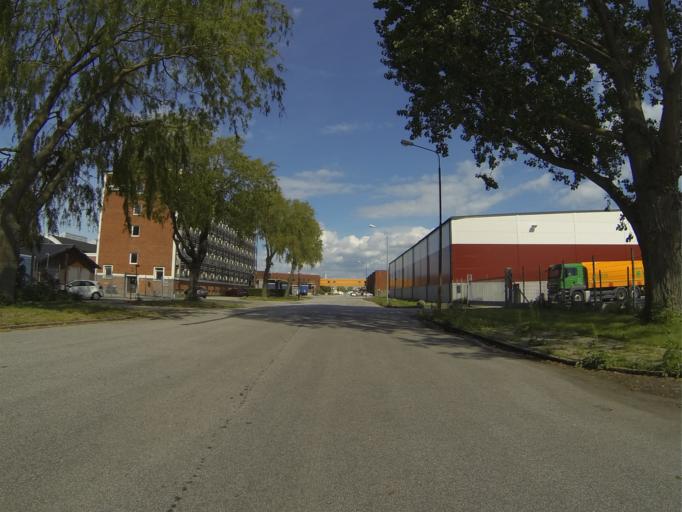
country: SE
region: Skane
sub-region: Malmo
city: Malmoe
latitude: 55.6199
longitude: 13.0269
